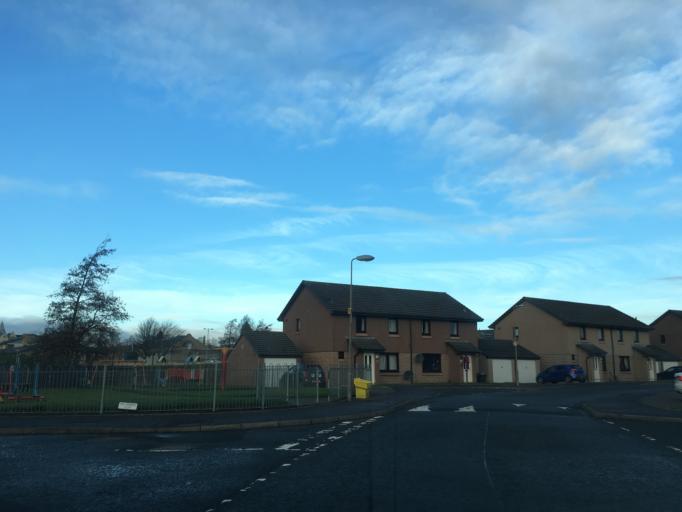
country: GB
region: Scotland
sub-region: Edinburgh
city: Colinton
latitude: 55.9096
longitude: -3.2415
